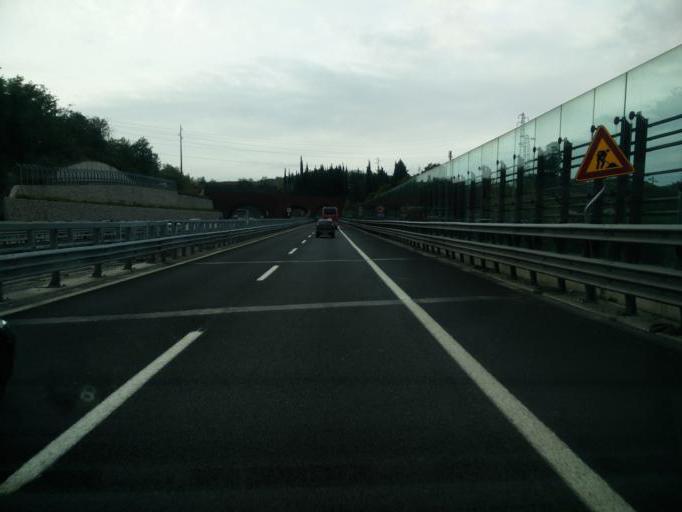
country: IT
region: Tuscany
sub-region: Province of Florence
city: Tavarnuzze
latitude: 43.7246
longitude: 11.2204
